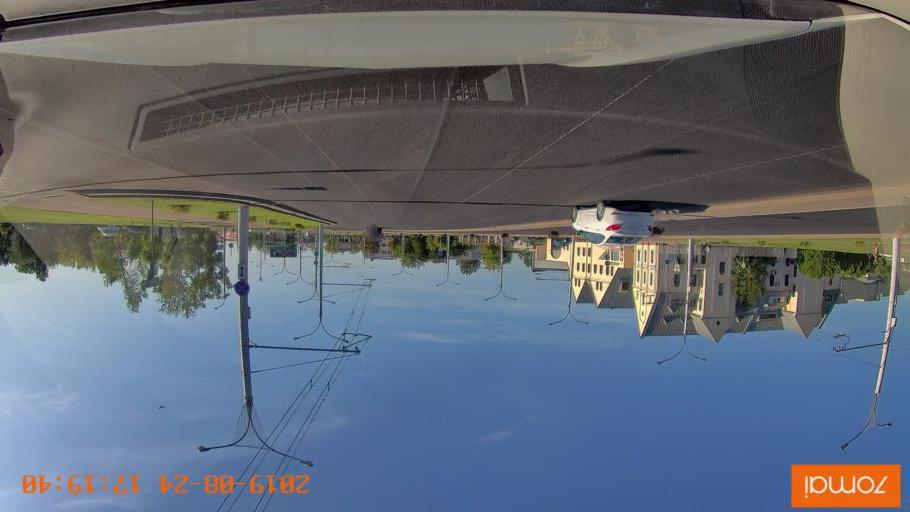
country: BY
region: Minsk
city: Vyaliki Trastsyanets
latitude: 53.8597
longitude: 27.6409
